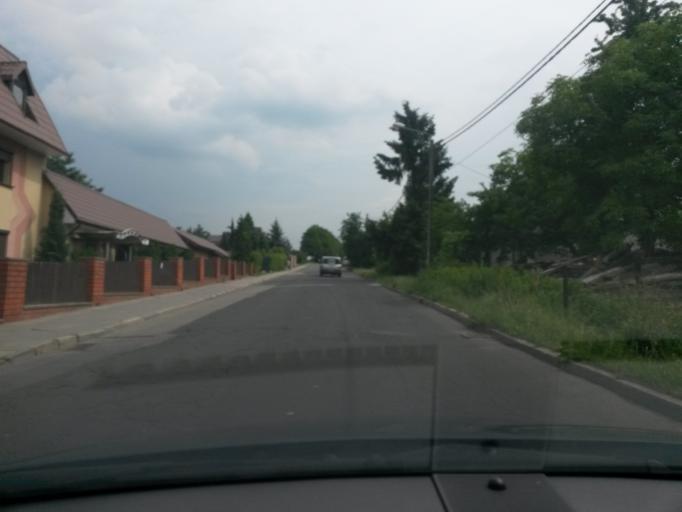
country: PL
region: Silesian Voivodeship
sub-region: Powiat czestochowski
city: Huta Stara B
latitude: 50.7663
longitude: 19.1526
